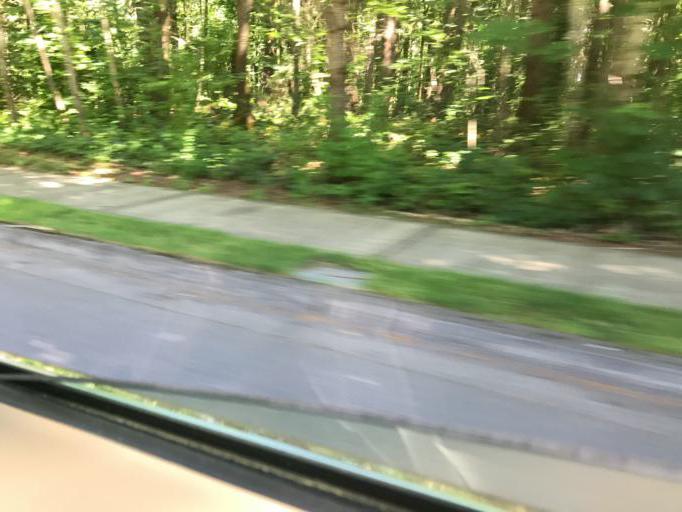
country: US
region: Washington
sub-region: King County
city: Redmond
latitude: 47.6264
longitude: -122.1275
